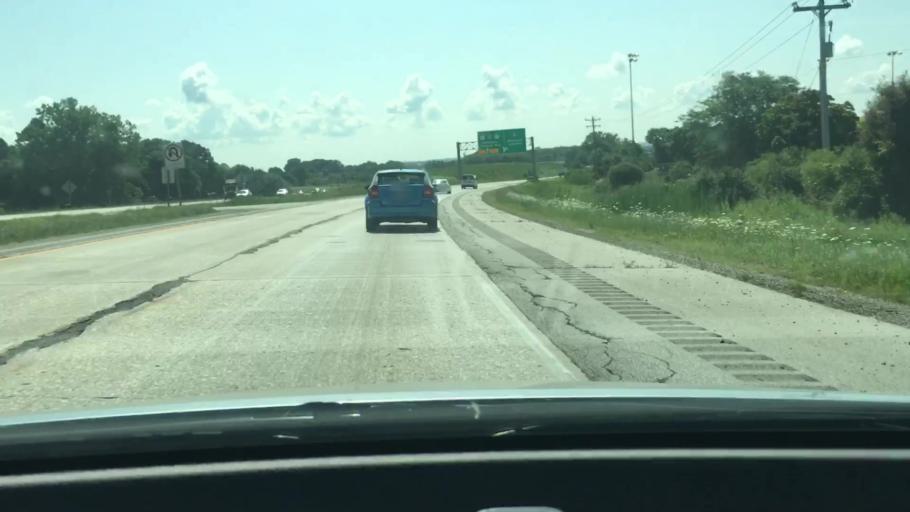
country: US
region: Wisconsin
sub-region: Brown County
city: Ashwaubenon
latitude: 44.4896
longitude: -88.0907
